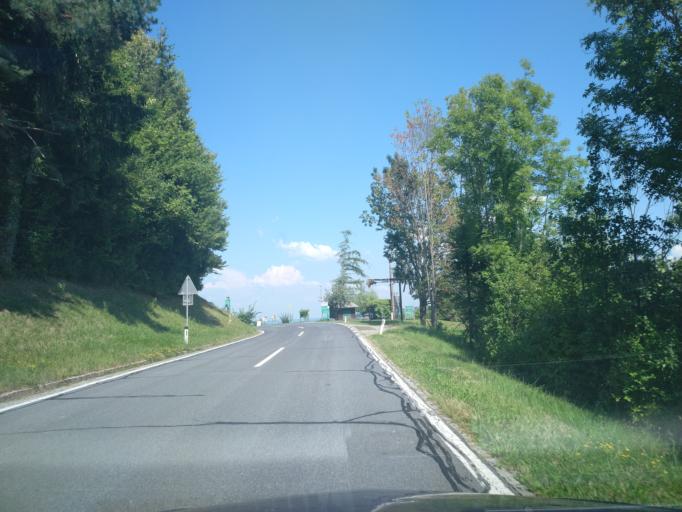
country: AT
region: Styria
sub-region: Politischer Bezirk Leibnitz
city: Leutschach
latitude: 46.6813
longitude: 15.4796
